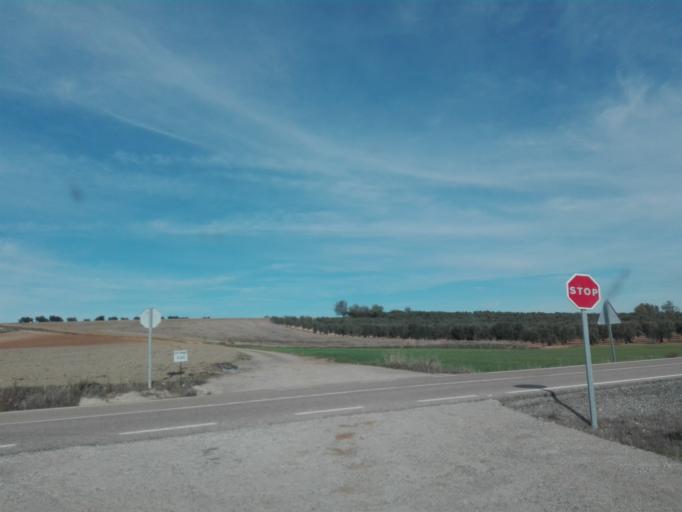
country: ES
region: Extremadura
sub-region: Provincia de Badajoz
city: Valverde de Llerena
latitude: 38.2481
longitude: -5.7617
